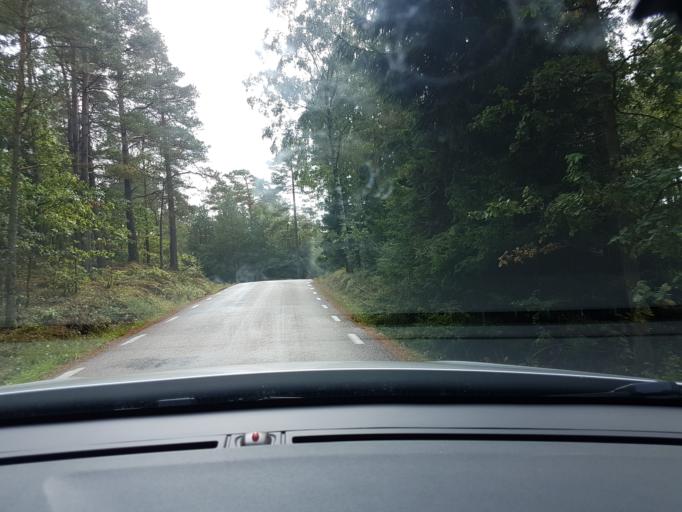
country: SE
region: Vaestra Goetaland
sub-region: Ale Kommun
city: Alvangen
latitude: 57.9062
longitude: 12.1737
